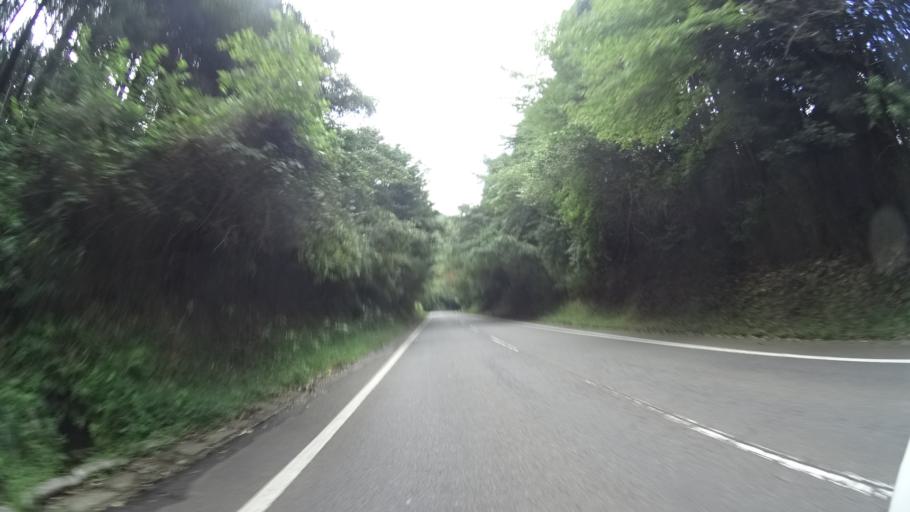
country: JP
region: Oita
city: Beppu
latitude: 33.3256
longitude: 131.4173
